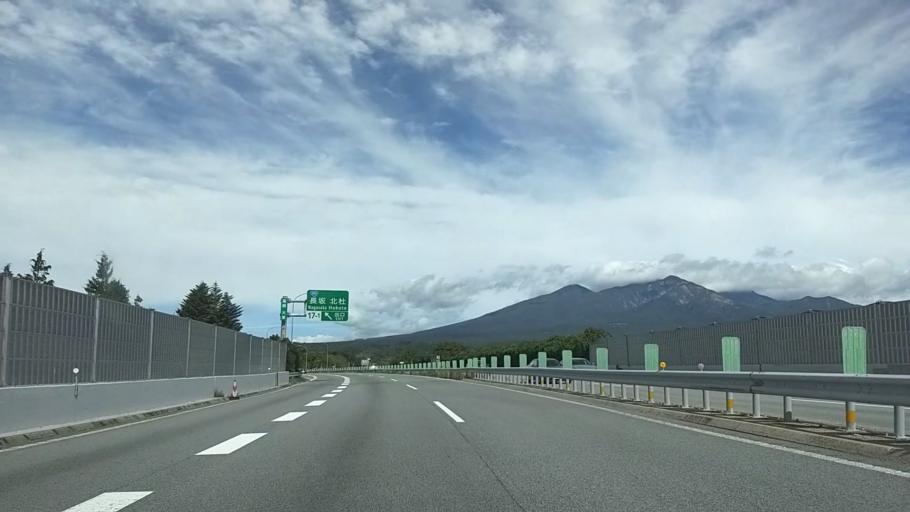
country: JP
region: Yamanashi
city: Nirasaki
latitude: 35.8336
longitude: 138.3915
